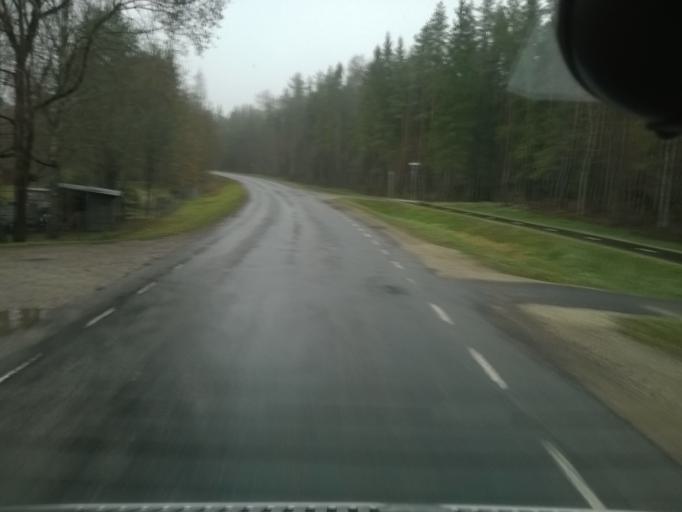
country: EE
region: Raplamaa
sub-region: Kohila vald
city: Kohila
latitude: 59.1737
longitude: 24.6559
